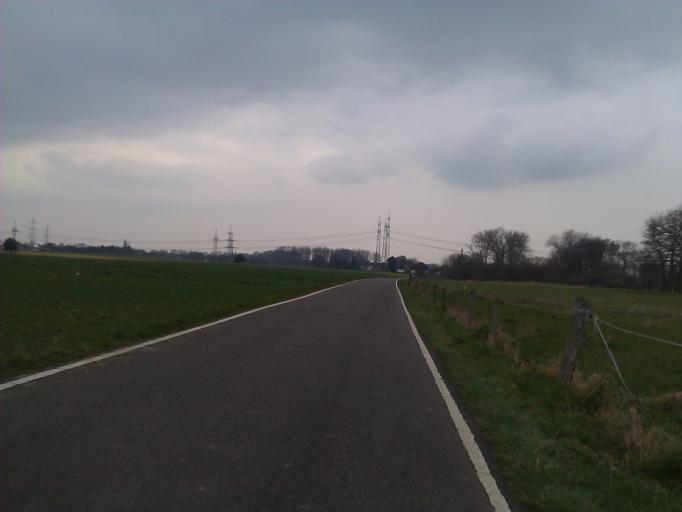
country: DE
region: North Rhine-Westphalia
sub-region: Regierungsbezirk Koln
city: Leverkusen
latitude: 51.0347
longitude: 6.9522
